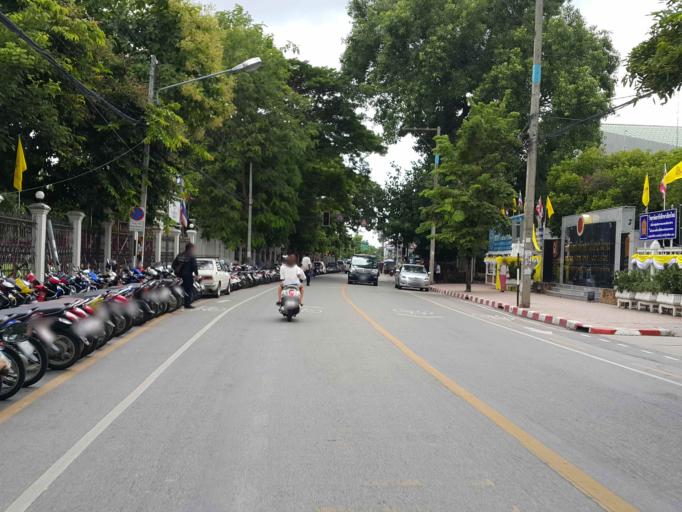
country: TH
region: Chiang Mai
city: Chiang Mai
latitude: 18.7925
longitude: 98.9878
